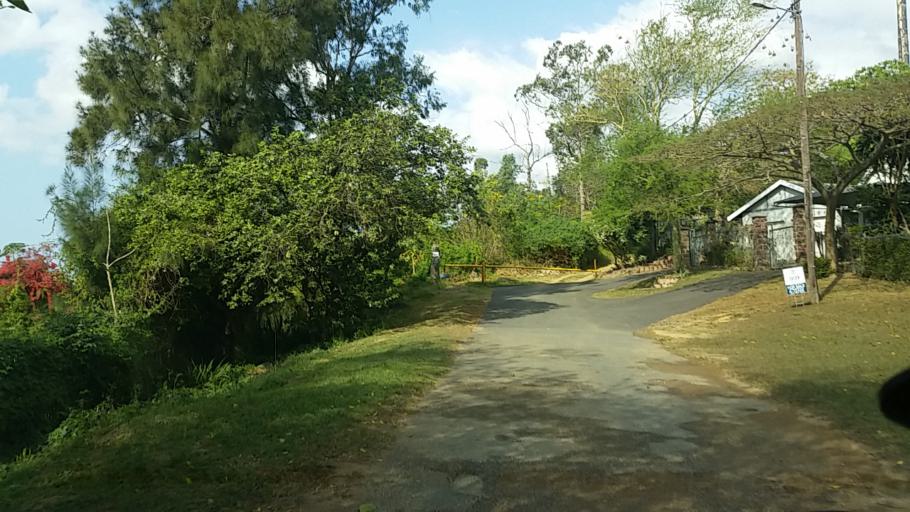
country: ZA
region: KwaZulu-Natal
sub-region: eThekwini Metropolitan Municipality
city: Berea
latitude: -29.8362
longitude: 30.9545
